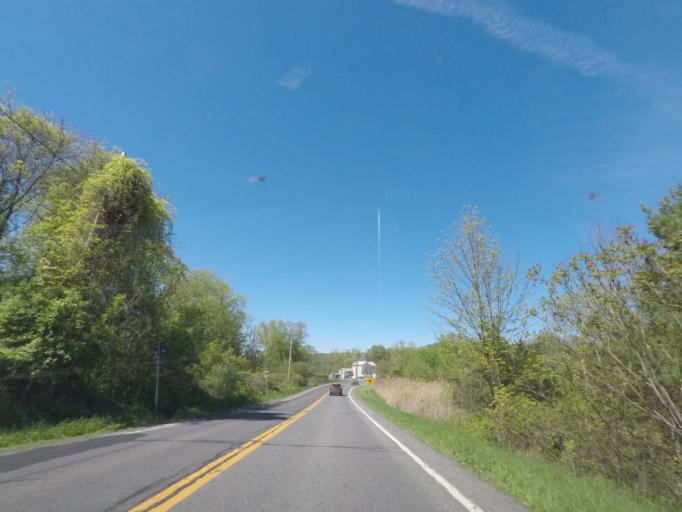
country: US
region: New York
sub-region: Ulster County
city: Saugerties
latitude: 42.1156
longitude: -73.9357
